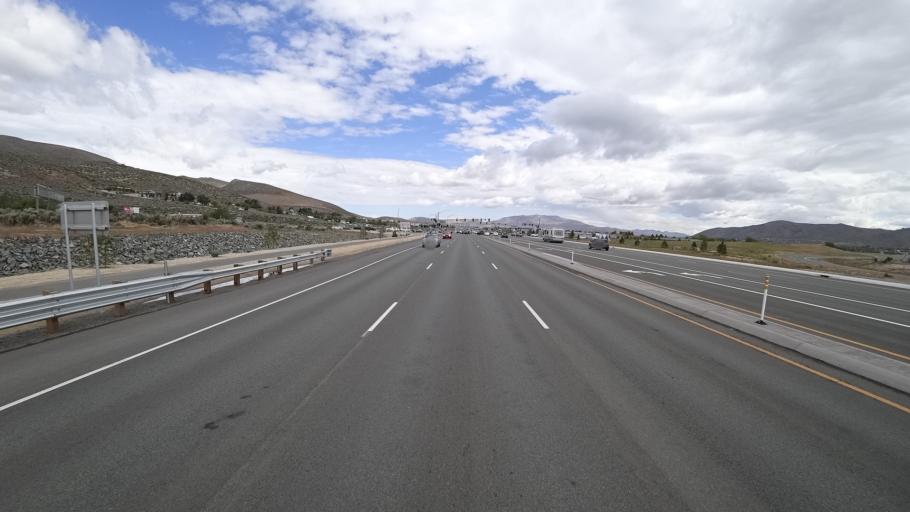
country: US
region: Nevada
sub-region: Douglas County
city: Indian Hills
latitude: 39.1192
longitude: -119.7723
